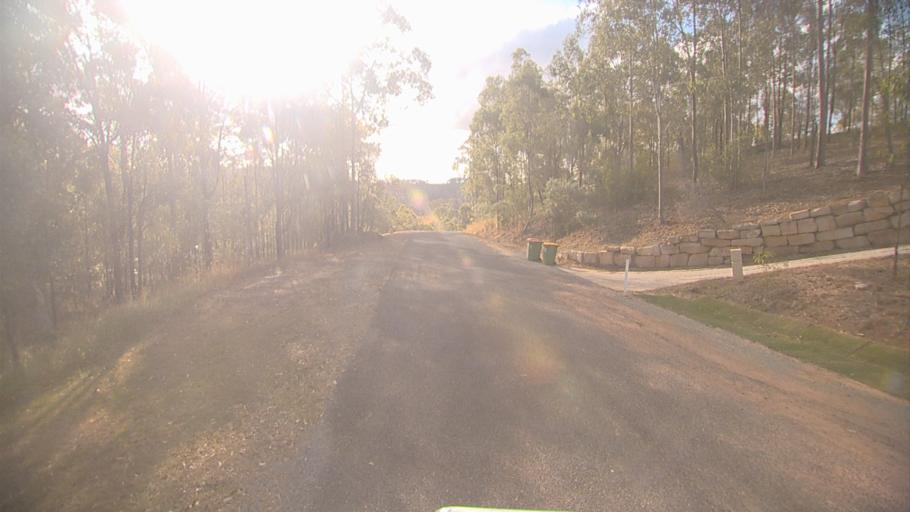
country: AU
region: Queensland
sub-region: Logan
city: Cedar Vale
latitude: -27.9082
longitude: 153.0641
